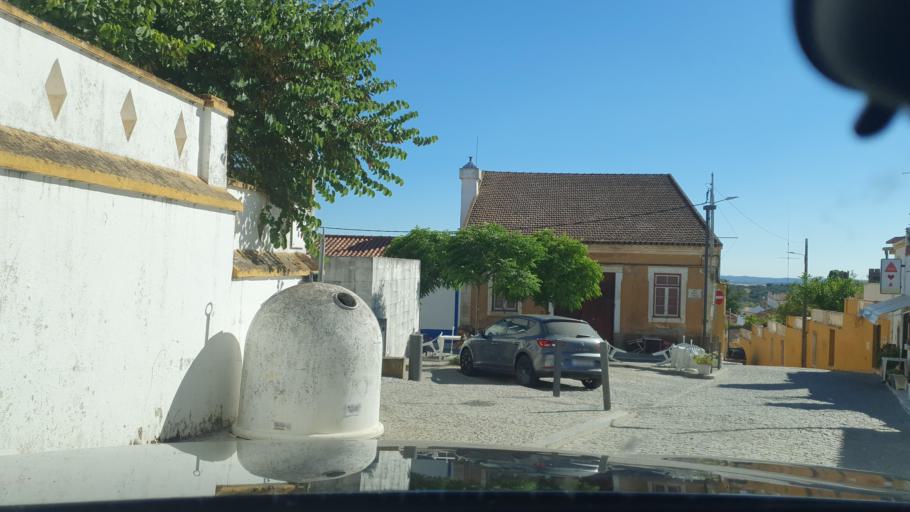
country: PT
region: Evora
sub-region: Alandroal
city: Alandroal
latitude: 38.7024
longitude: -7.4014
